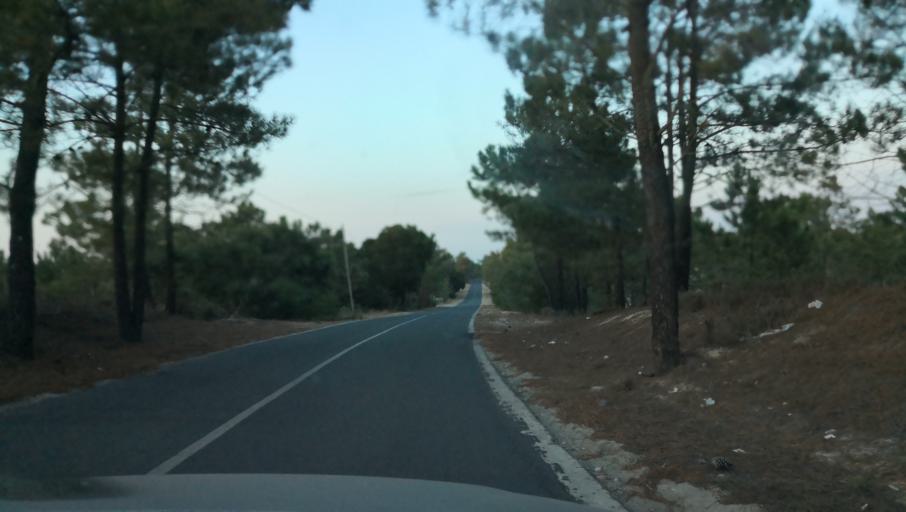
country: PT
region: Setubal
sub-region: Setubal
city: Setubal
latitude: 38.3867
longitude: -8.7828
